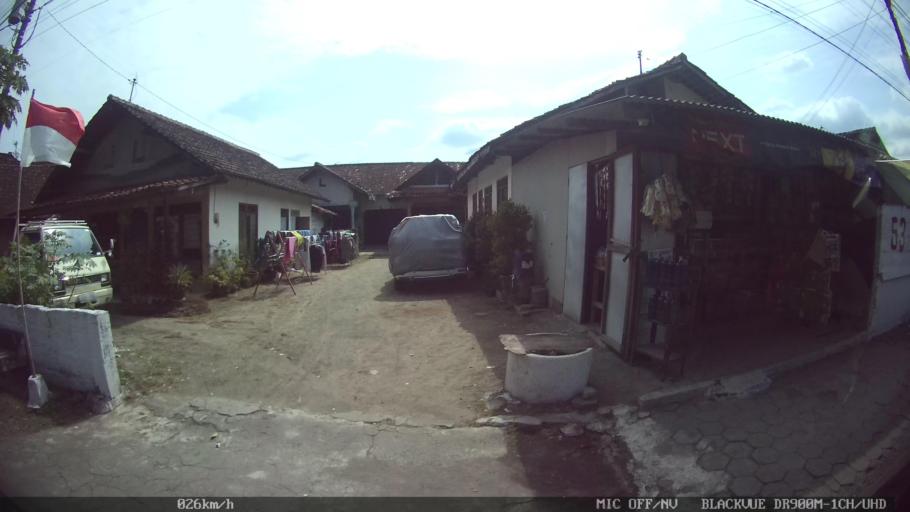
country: ID
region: Daerah Istimewa Yogyakarta
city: Depok
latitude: -7.7751
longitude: 110.4356
